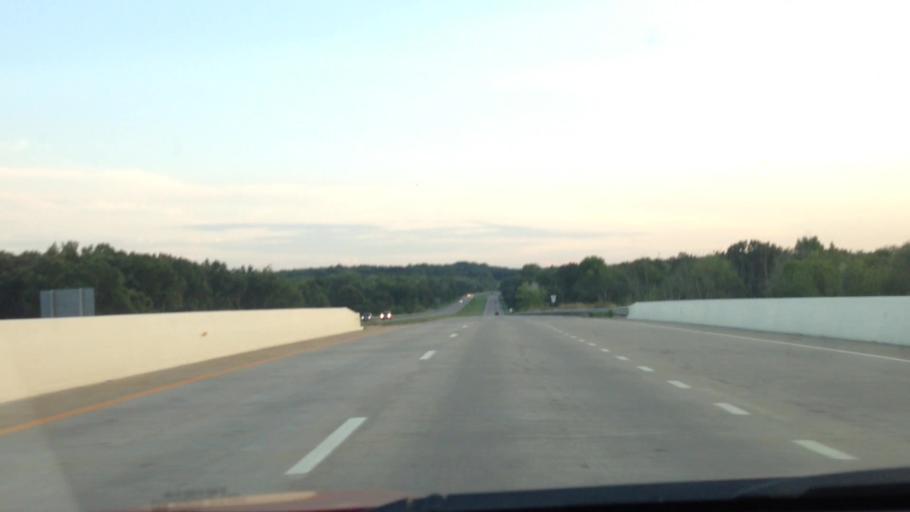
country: US
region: Ohio
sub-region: Summit County
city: Fairlawn
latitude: 41.0967
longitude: -81.6583
